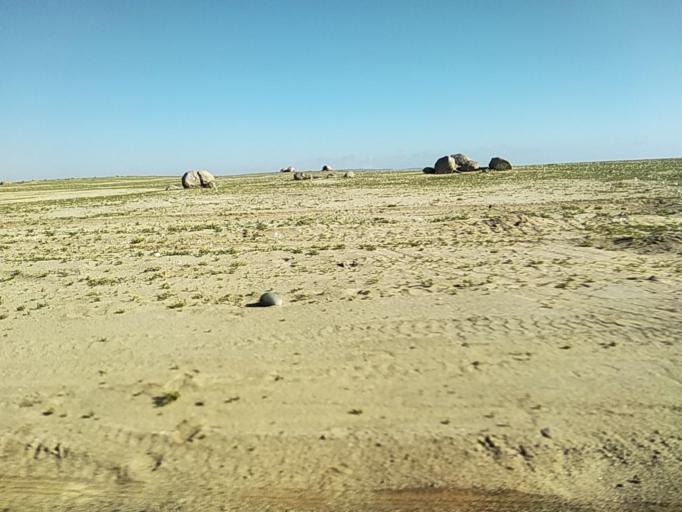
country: CL
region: Atacama
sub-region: Provincia de Copiapo
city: Copiapo
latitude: -27.3161
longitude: -70.8744
